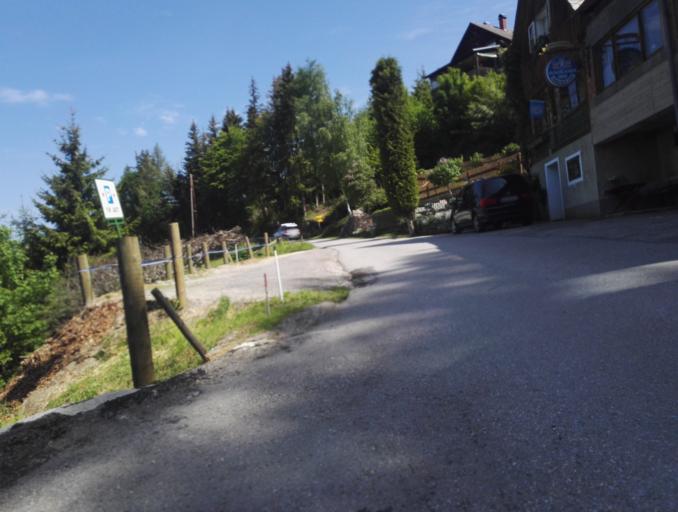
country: AT
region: Styria
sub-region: Politischer Bezirk Graz-Umgebung
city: Semriach
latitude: 47.1905
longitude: 15.4282
